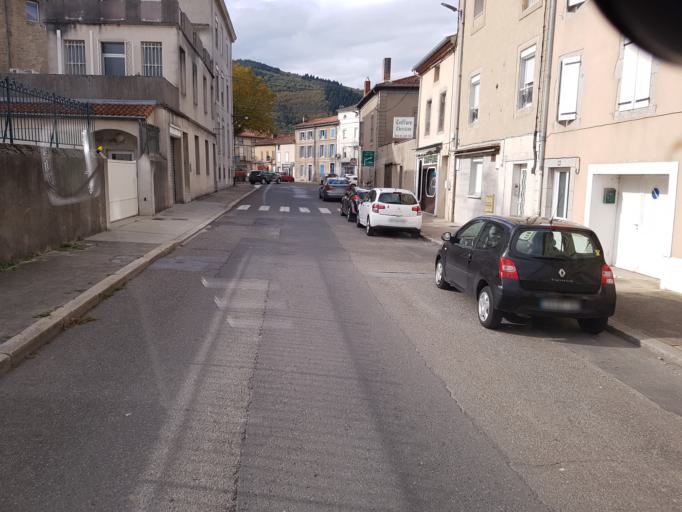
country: FR
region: Midi-Pyrenees
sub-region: Departement du Tarn
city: Mazamet
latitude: 43.4942
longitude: 2.3786
